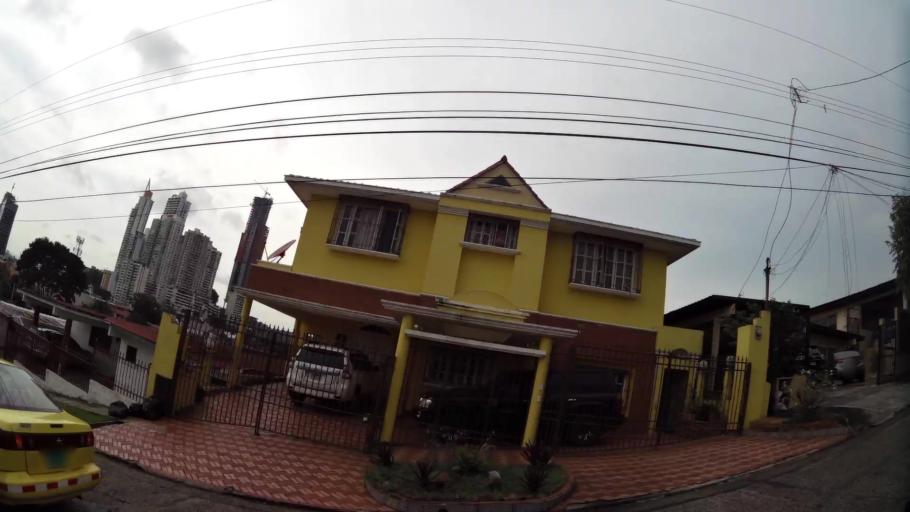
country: PA
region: Panama
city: Panama
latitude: 9.0088
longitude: -79.5321
